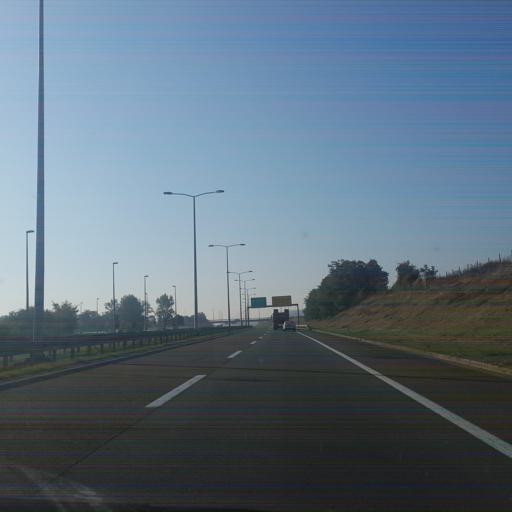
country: RS
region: Central Serbia
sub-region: Nisavski Okrug
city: Merosina
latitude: 43.2851
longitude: 21.8006
